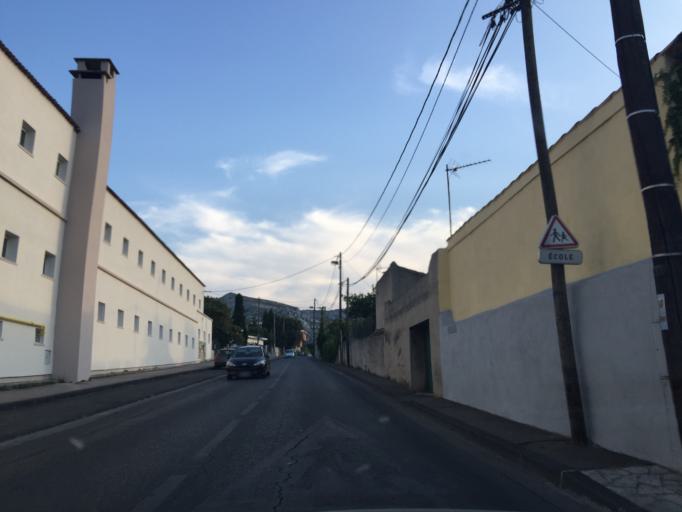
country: FR
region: Provence-Alpes-Cote d'Azur
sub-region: Departement des Bouches-du-Rhone
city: Marseille 09
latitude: 43.2351
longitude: 5.4106
